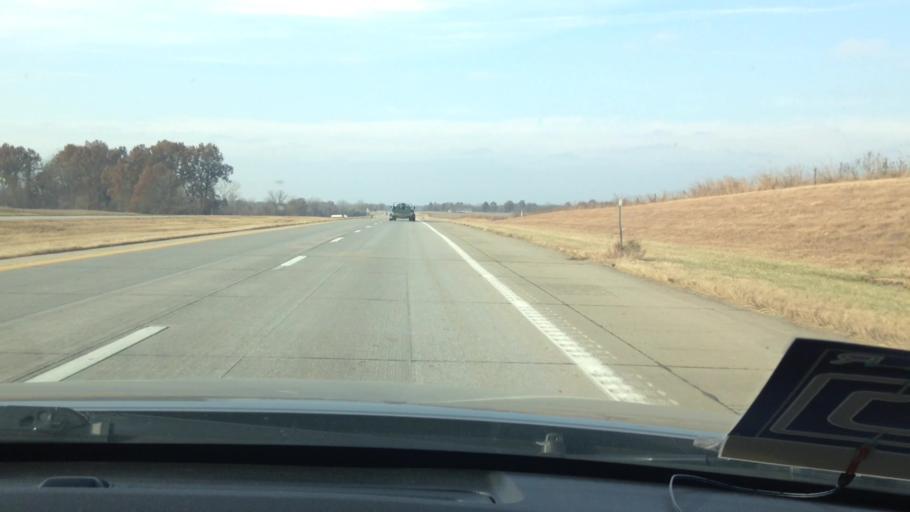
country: US
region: Missouri
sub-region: Henry County
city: Clinton
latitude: 38.4444
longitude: -93.9549
